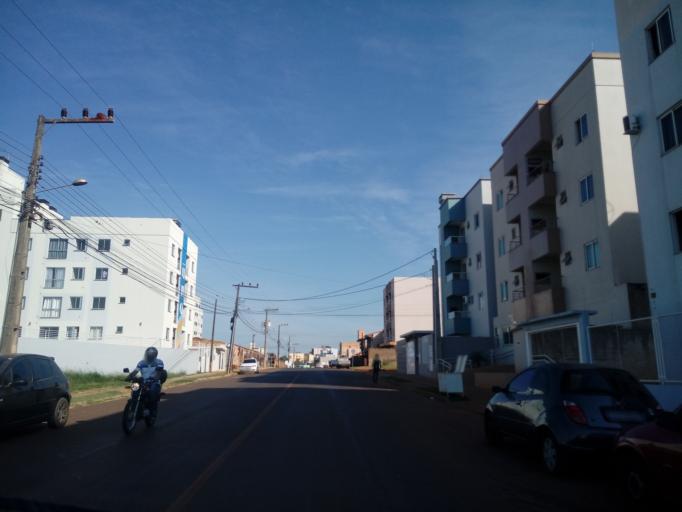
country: BR
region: Santa Catarina
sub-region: Chapeco
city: Chapeco
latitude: -27.0950
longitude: -52.6694
